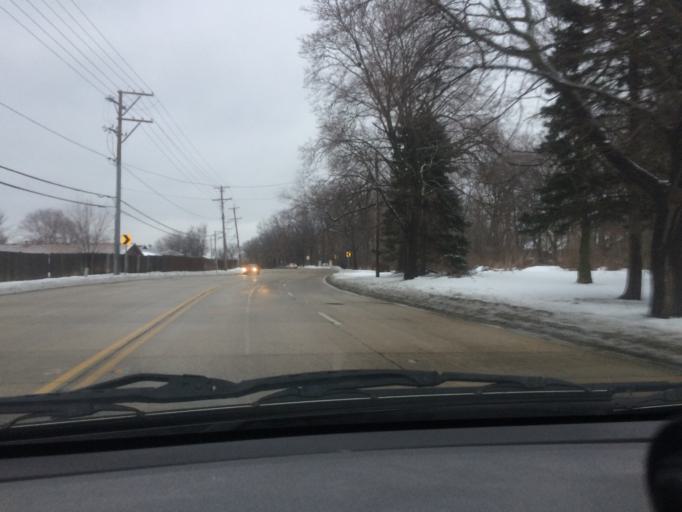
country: US
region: Illinois
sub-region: Cook County
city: Bartlett
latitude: 42.0099
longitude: -88.1845
